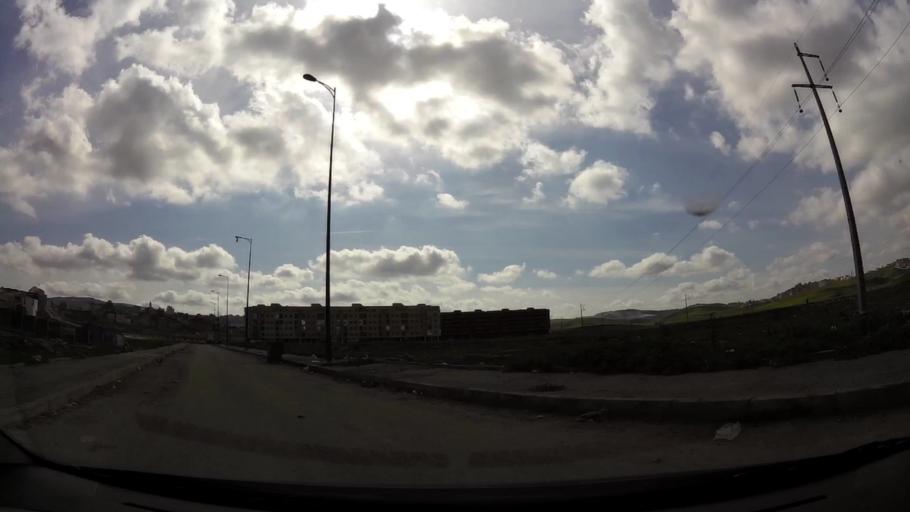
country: MA
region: Tanger-Tetouan
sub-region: Tanger-Assilah
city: Tangier
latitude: 35.7644
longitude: -5.7727
